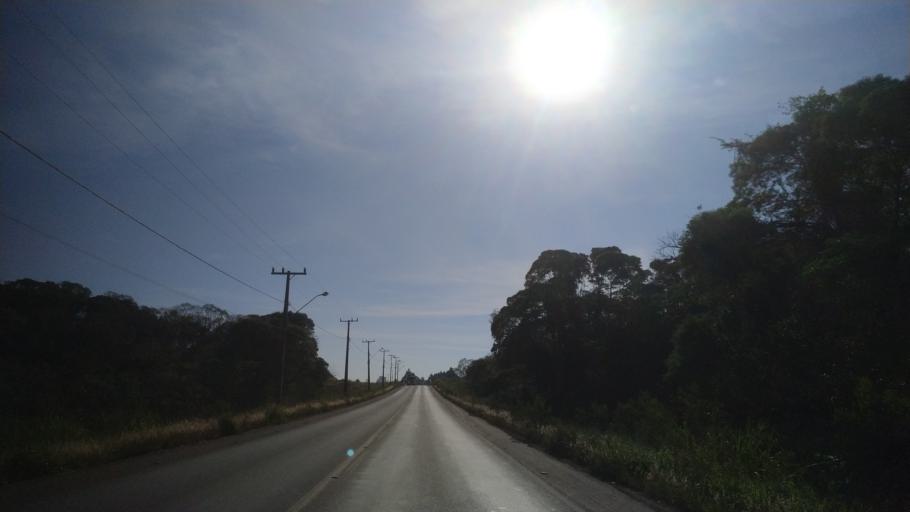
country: BR
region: Santa Catarina
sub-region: Chapeco
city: Chapeco
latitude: -27.1206
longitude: -52.6333
